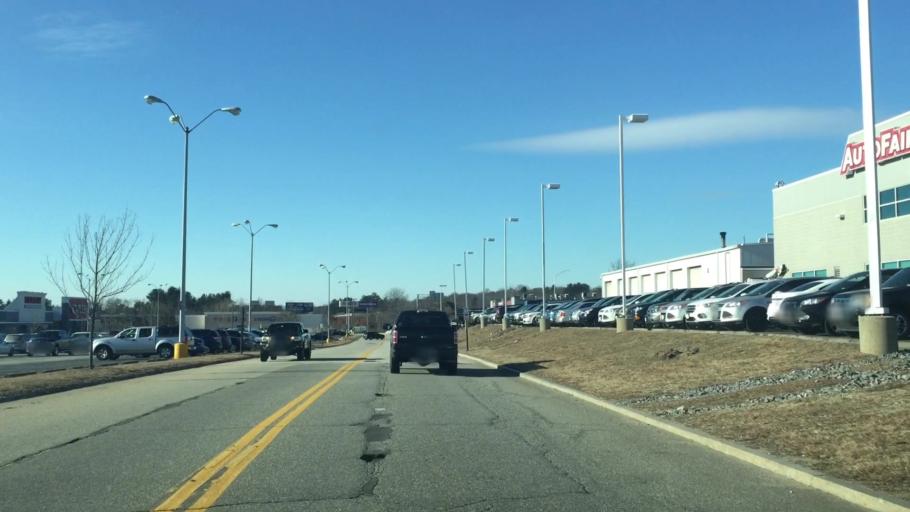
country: US
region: New Hampshire
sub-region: Hillsborough County
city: Manchester
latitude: 42.9547
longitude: -71.4384
